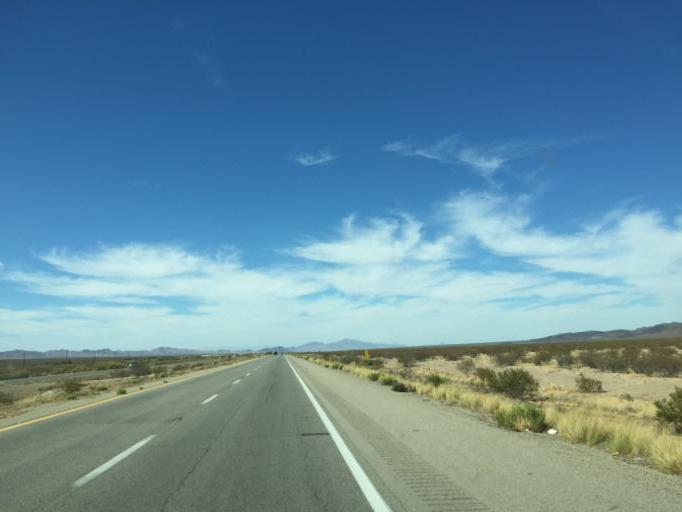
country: US
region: Arizona
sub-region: Mohave County
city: Dolan Springs
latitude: 35.5970
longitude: -114.3988
